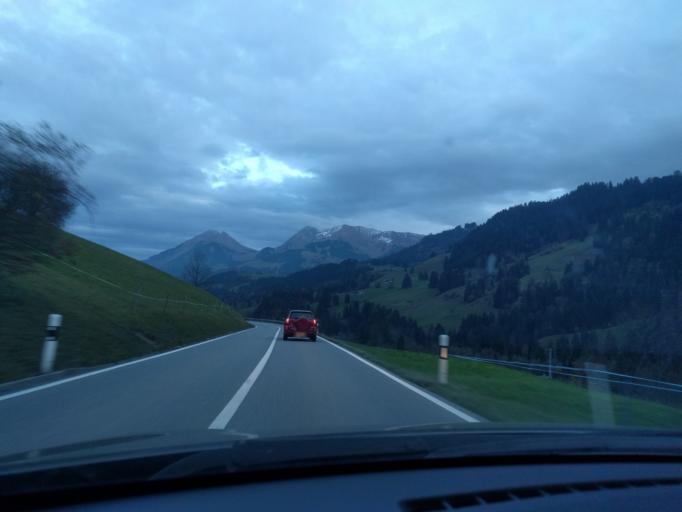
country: CH
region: Bern
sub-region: Frutigen-Niedersimmental District
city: Erlenbach im Simmental
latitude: 46.6581
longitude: 7.5117
